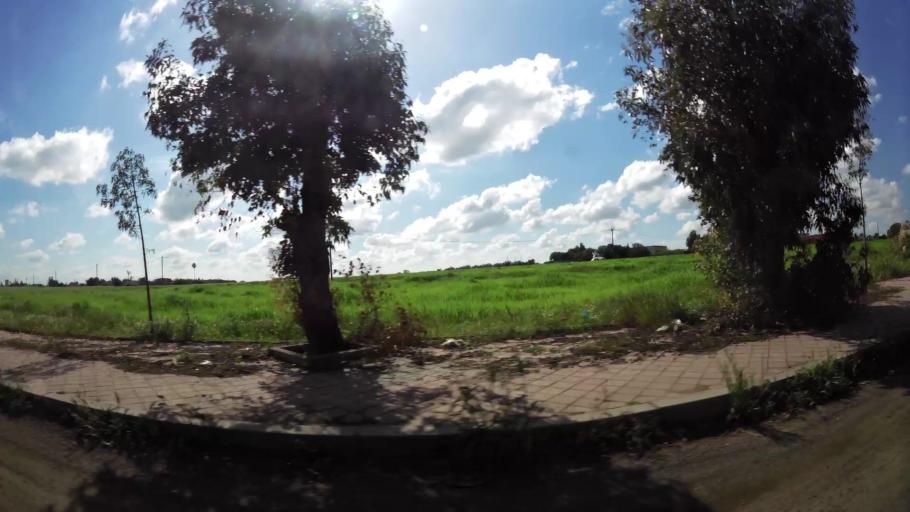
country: MA
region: Grand Casablanca
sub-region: Mediouna
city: Mediouna
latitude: 33.4457
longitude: -7.5209
